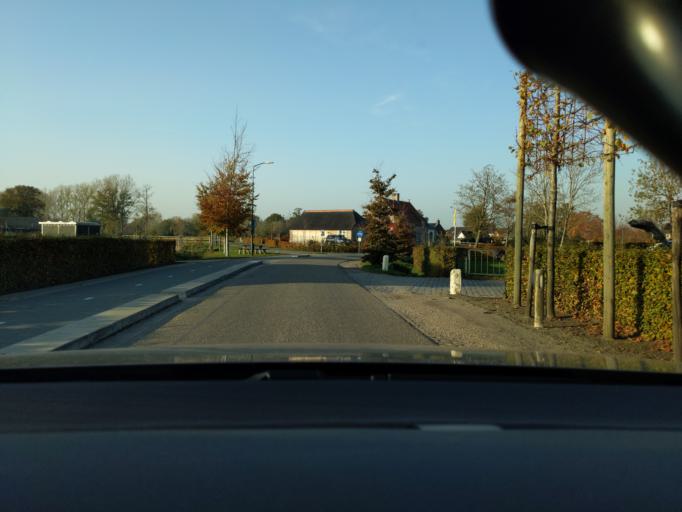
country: NL
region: North Brabant
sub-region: Gemeente Sint-Oedenrode
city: Sint-Oedenrode
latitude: 51.5698
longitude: 5.4303
